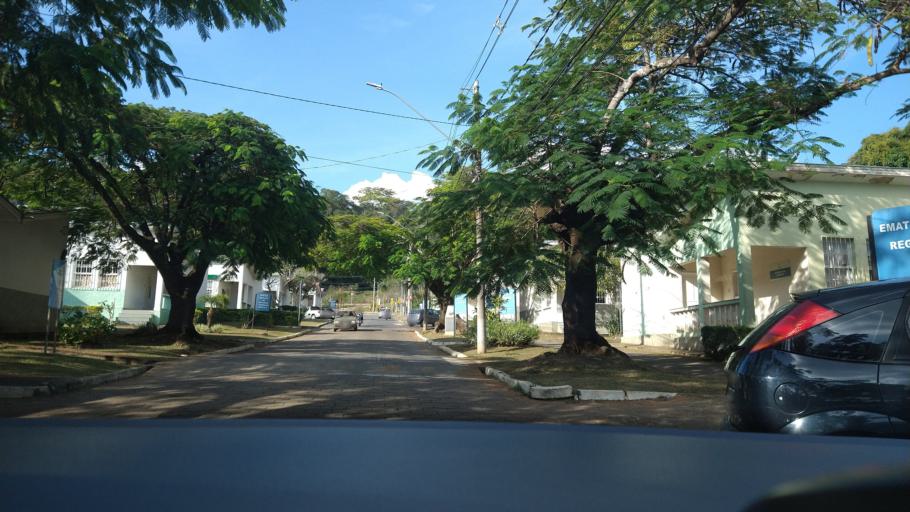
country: BR
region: Minas Gerais
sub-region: Vicosa
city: Vicosa
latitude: -20.7544
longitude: -42.8723
